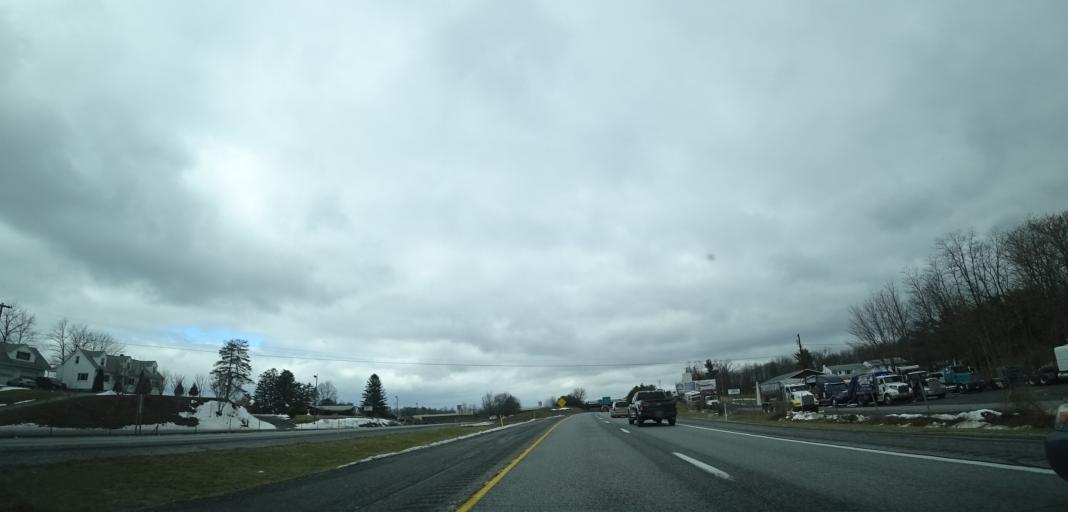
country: US
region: Pennsylvania
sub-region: Bedford County
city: Earlston
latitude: 39.9820
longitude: -78.2440
